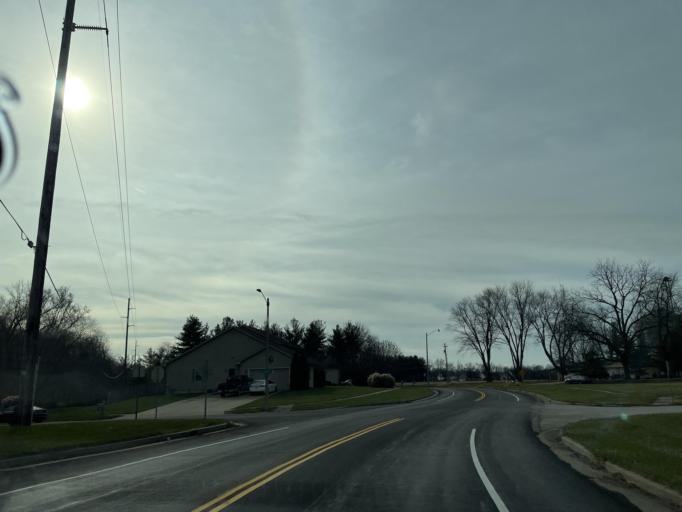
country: US
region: Illinois
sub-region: Sangamon County
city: Leland Grove
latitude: 39.7819
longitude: -89.7339
